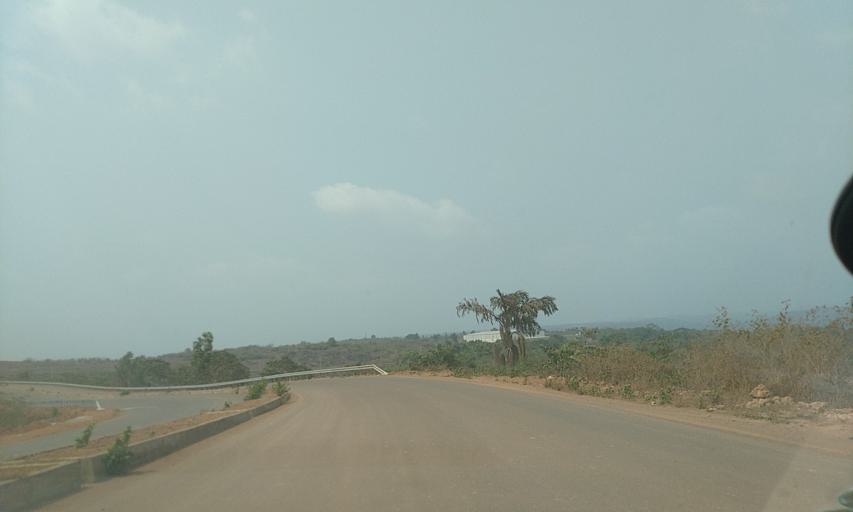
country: IN
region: Goa
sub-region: North Goa
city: Queula
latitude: 15.3527
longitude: 73.9645
